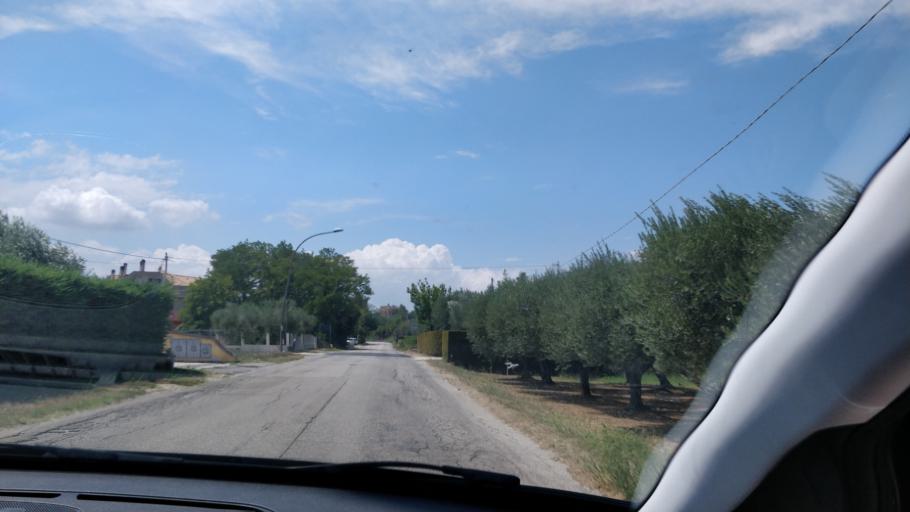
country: IT
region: Abruzzo
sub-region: Provincia di Chieti
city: Francavilla al Mare
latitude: 42.4229
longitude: 14.2523
